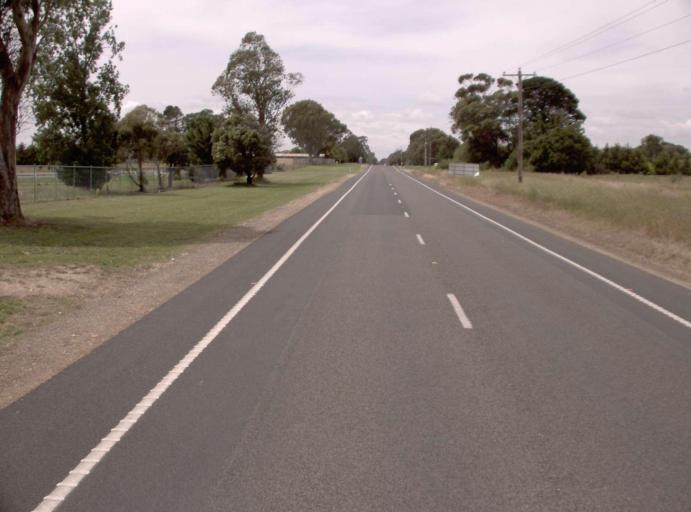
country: AU
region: Victoria
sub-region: Wellington
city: Sale
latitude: -38.0762
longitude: 147.0450
